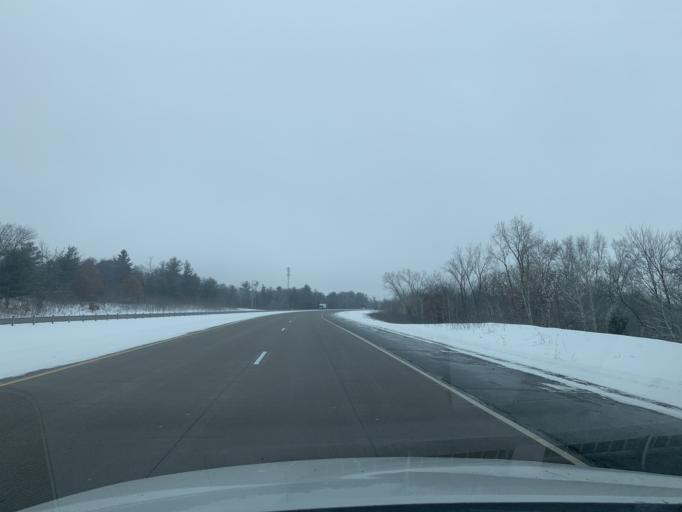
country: US
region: Minnesota
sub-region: Chisago County
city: Harris
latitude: 45.5903
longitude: -92.9951
